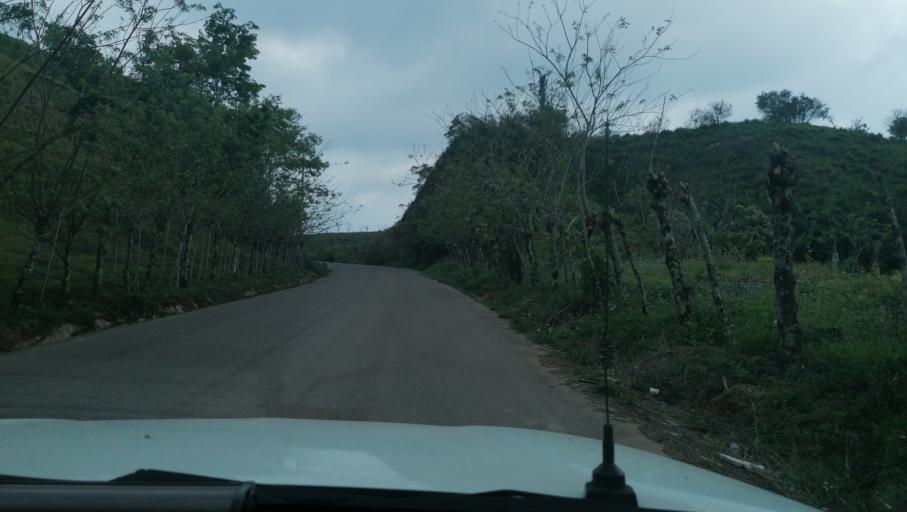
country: MX
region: Chiapas
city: Tecpatan
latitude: 17.1926
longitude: -93.3486
